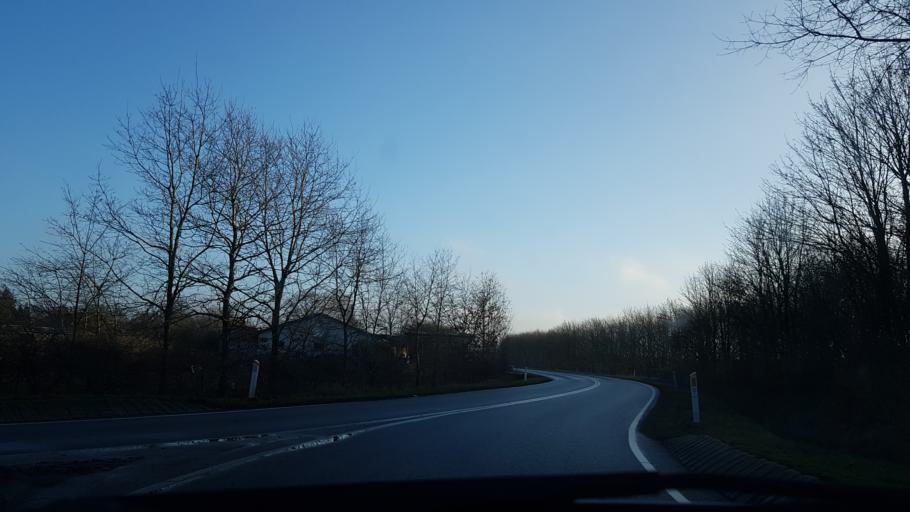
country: DK
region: South Denmark
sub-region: Haderslev Kommune
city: Vojens
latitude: 55.1986
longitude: 9.1969
